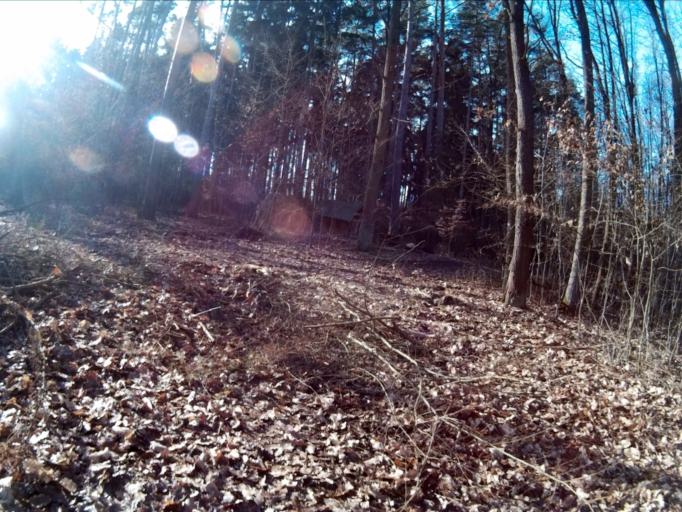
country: CZ
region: Vysocina
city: Mohelno
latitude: 49.1408
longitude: 16.2021
